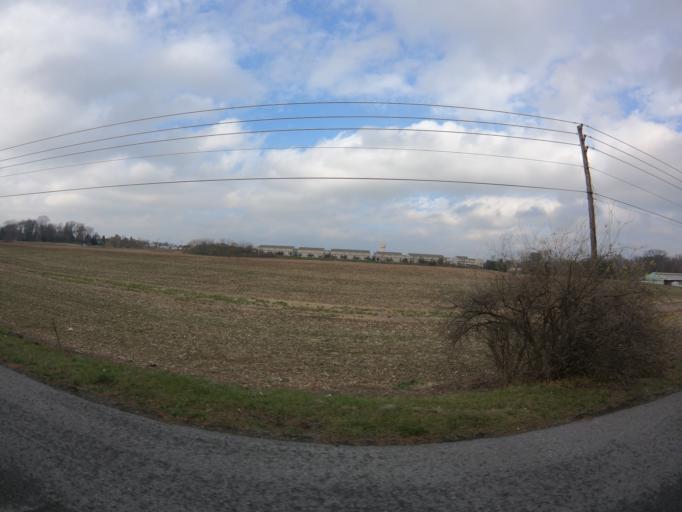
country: US
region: Pennsylvania
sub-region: Lancaster County
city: Marietta
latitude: 40.0608
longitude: -76.5640
